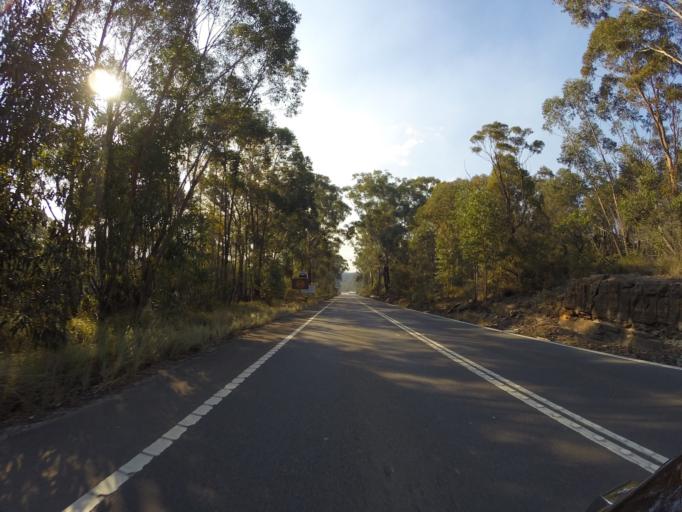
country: AU
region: New South Wales
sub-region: Liverpool
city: East Hills
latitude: -33.9867
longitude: 150.9924
